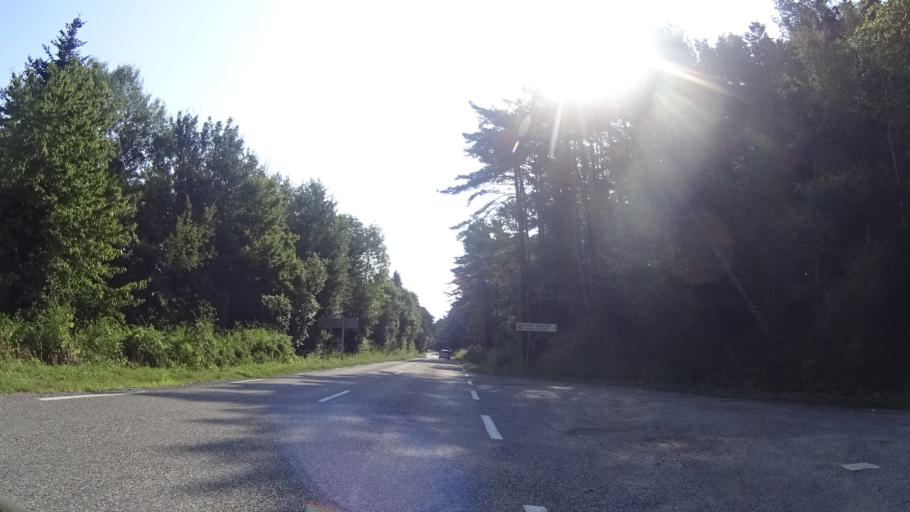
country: FR
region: Midi-Pyrenees
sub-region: Departement de l'Ariege
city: Belesta
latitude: 42.9114
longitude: 1.9875
